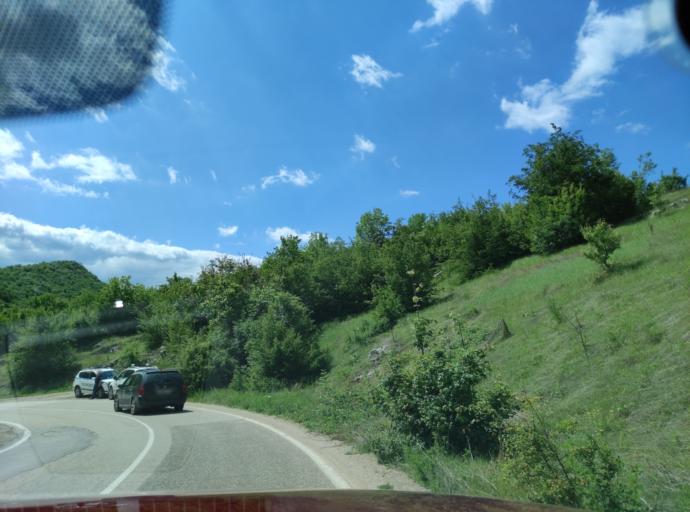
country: BG
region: Montana
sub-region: Obshtina Chiprovtsi
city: Chiprovtsi
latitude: 43.4925
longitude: 22.8032
